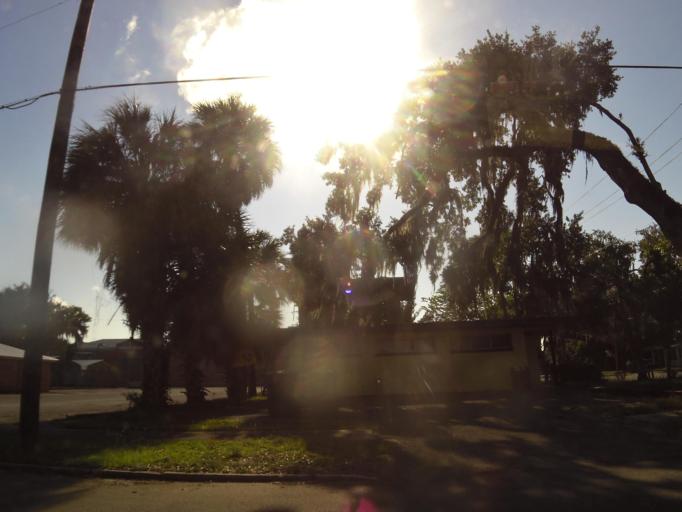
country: US
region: Florida
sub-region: Putnam County
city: Palatka
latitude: 29.6485
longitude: -81.6307
